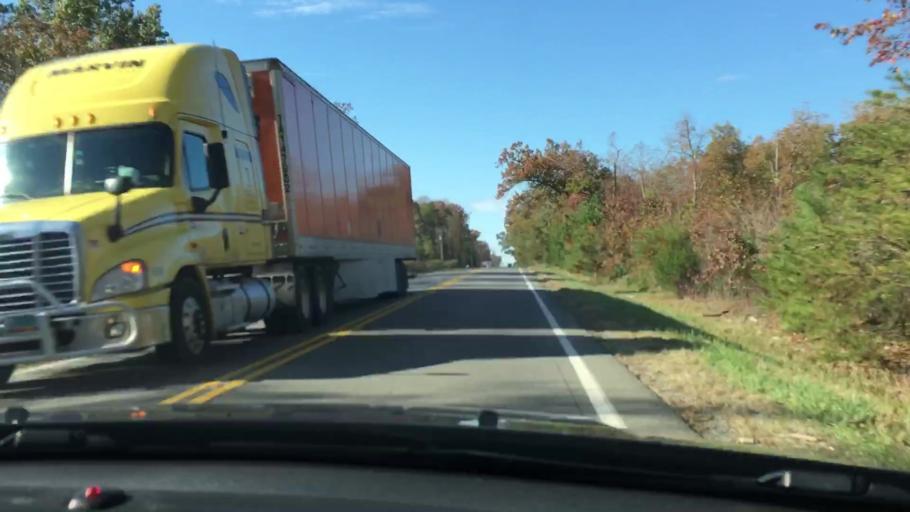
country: US
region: Virginia
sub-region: King William County
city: King William
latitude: 37.7157
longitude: -77.0681
